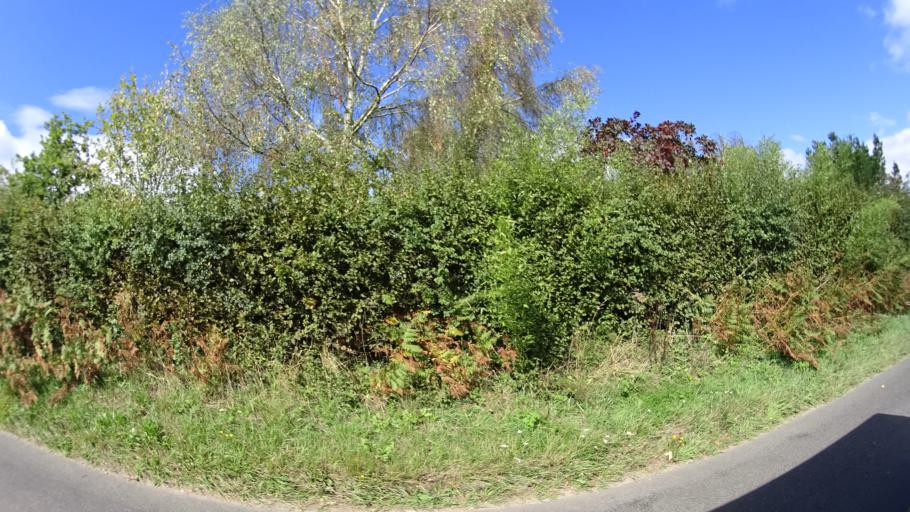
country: GB
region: England
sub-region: Hampshire
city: Romsey
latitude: 51.0135
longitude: -1.5326
